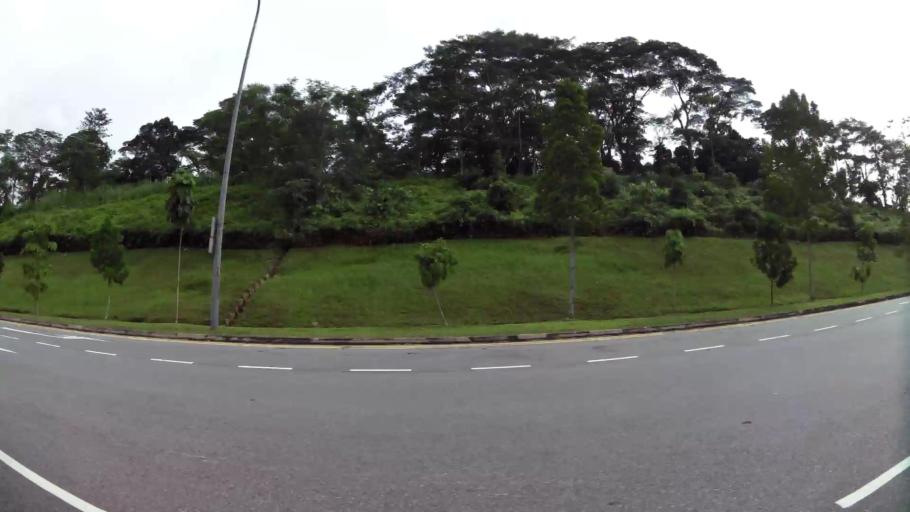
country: MY
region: Johor
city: Johor Bahru
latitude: 1.4163
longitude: 103.7648
